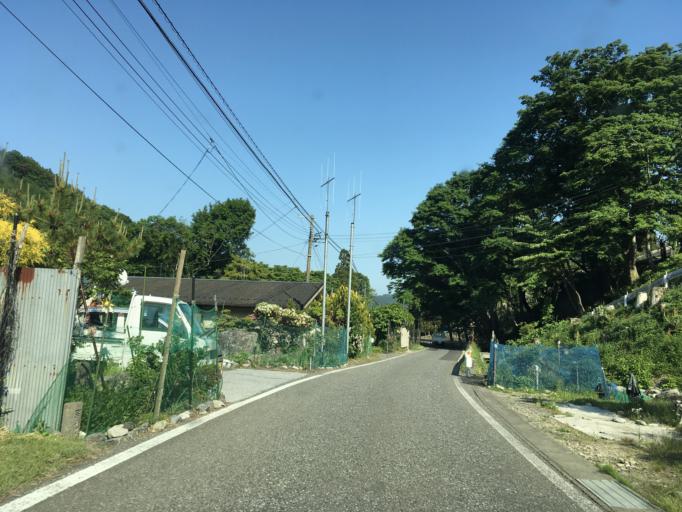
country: JP
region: Iwate
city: Kamaishi
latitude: 39.1977
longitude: 141.8295
